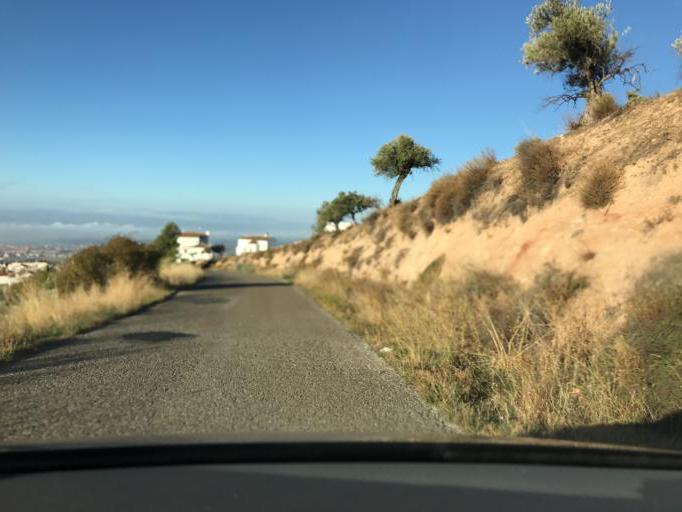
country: ES
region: Andalusia
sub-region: Provincia de Granada
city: Viznar
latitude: 37.2341
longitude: -3.5490
